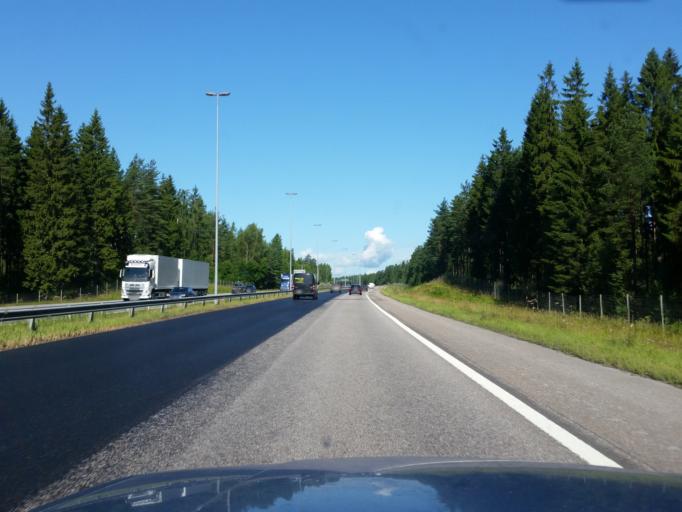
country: FI
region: Uusimaa
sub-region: Helsinki
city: Espoo
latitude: 60.2490
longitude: 24.5412
